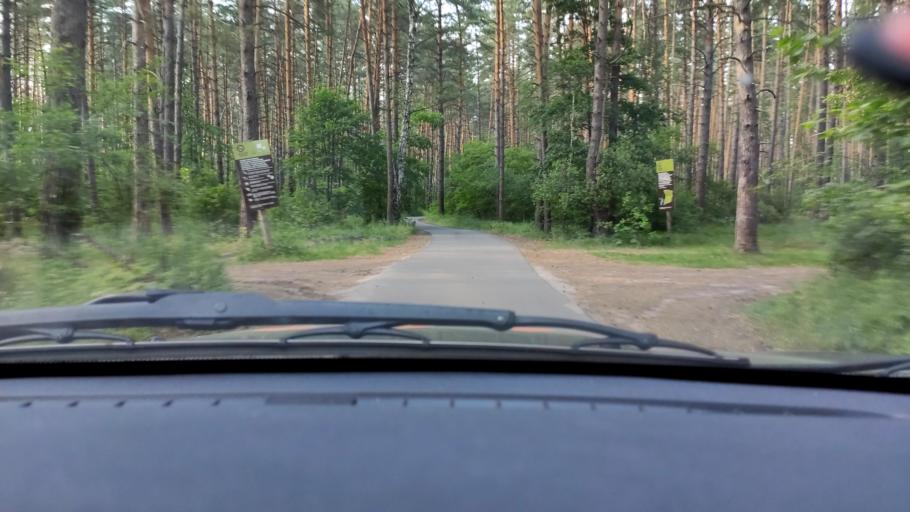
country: RU
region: Voronezj
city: Somovo
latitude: 51.7960
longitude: 39.3808
